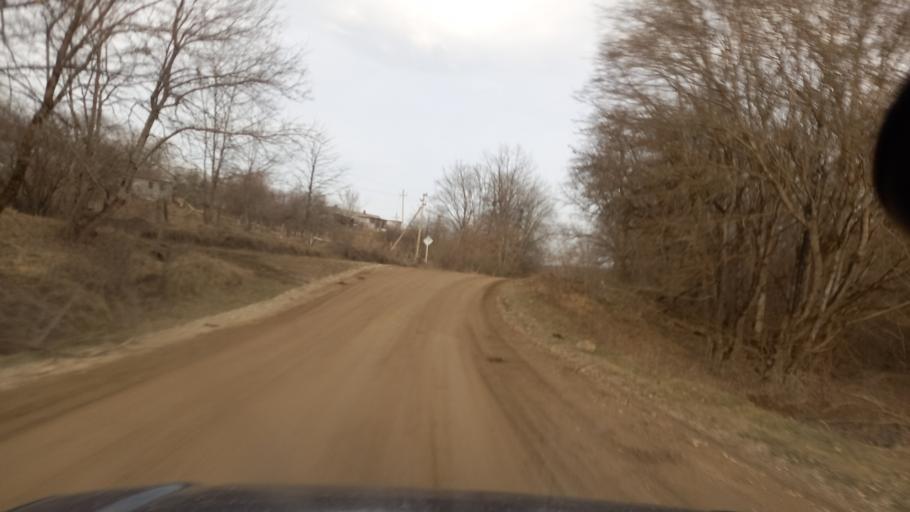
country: RU
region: Adygeya
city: Kamennomostskiy
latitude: 44.1649
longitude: 40.2449
